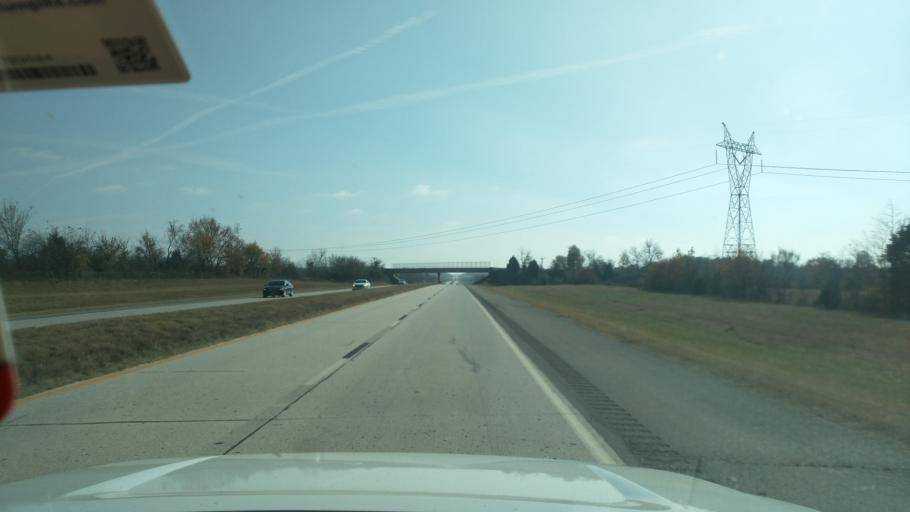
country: US
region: Oklahoma
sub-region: Muskogee County
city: Warner
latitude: 35.5687
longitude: -95.2476
